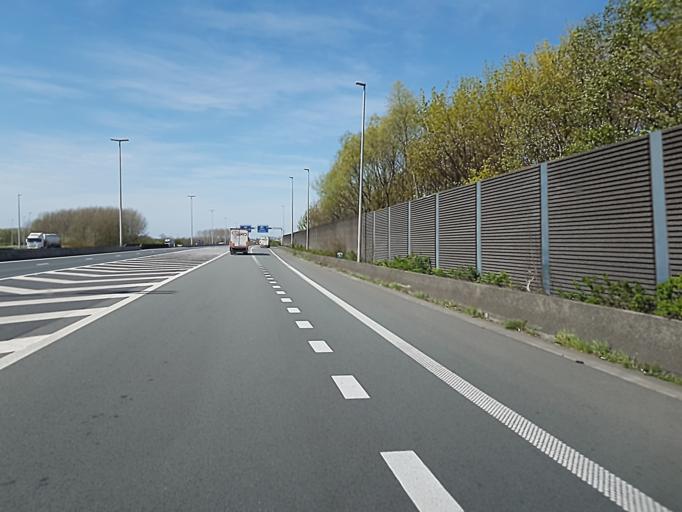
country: BE
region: Wallonia
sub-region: Province du Hainaut
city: Mouscron
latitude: 50.7854
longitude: 3.2370
